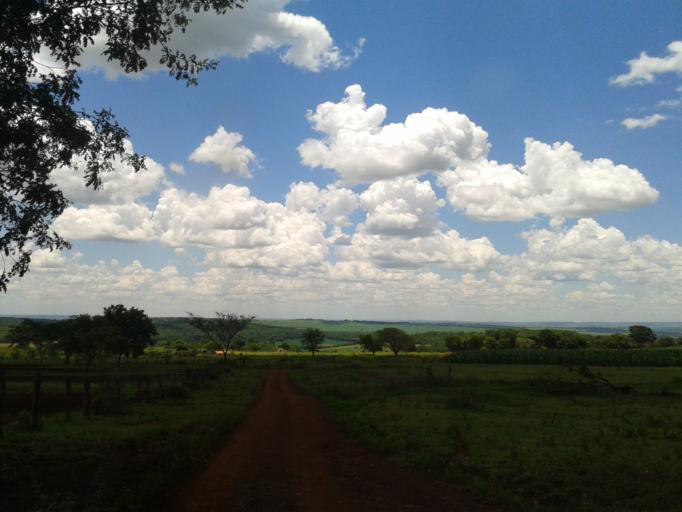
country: BR
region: Minas Gerais
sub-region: Centralina
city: Centralina
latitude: -18.6955
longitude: -49.1926
